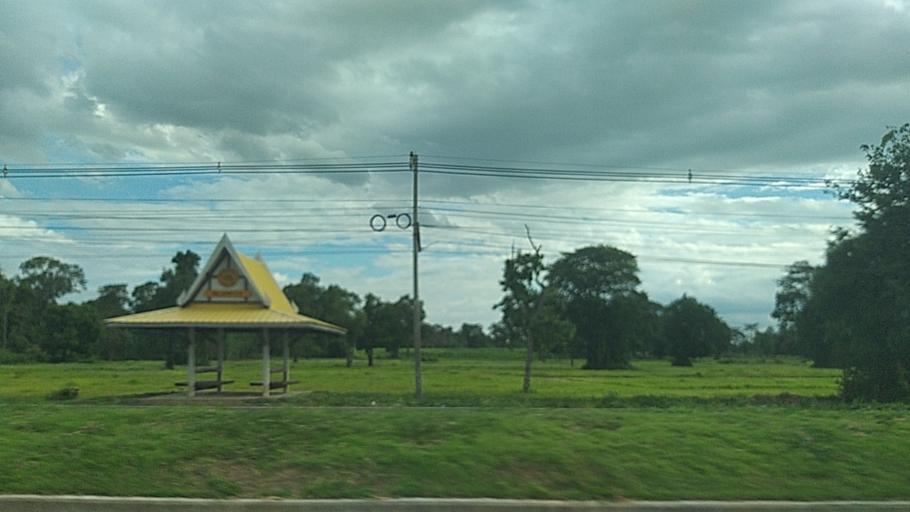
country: TH
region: Surin
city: Prasat
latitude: 14.5935
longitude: 103.4460
